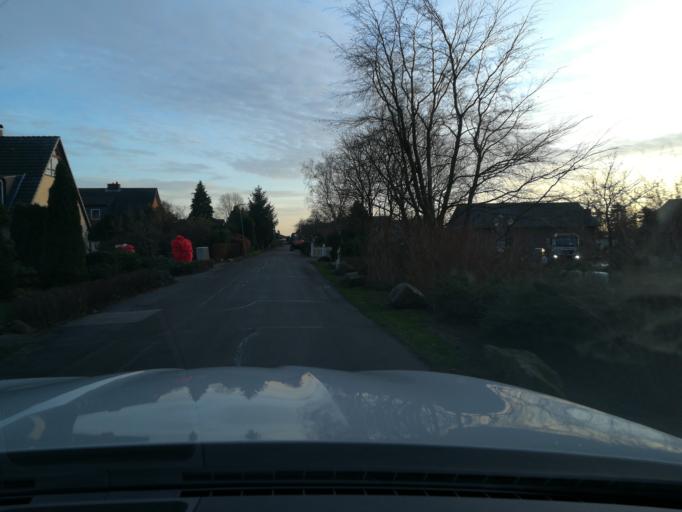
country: DE
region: Lower Saxony
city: Stelle
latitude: 53.4428
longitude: 10.0813
